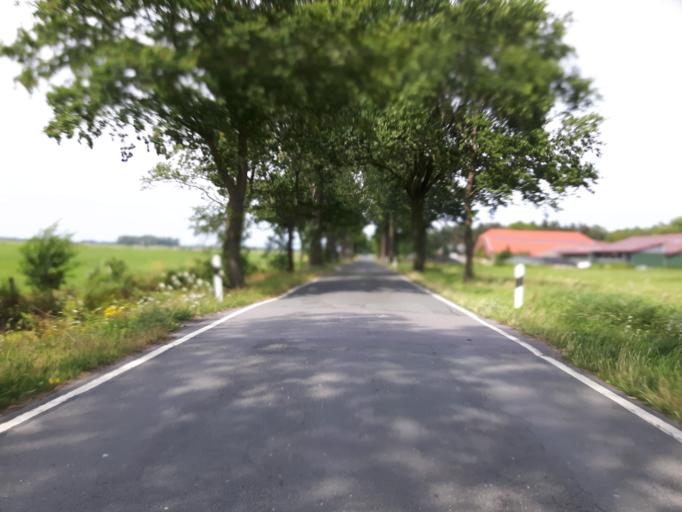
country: DE
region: Lower Saxony
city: Rastede
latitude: 53.3268
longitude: 8.2748
